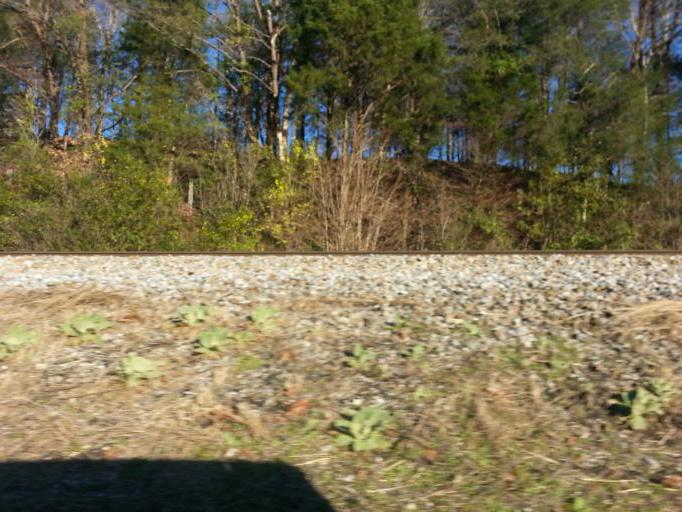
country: US
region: Tennessee
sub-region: Anderson County
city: Oak Ridge
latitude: 36.0681
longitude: -84.2461
